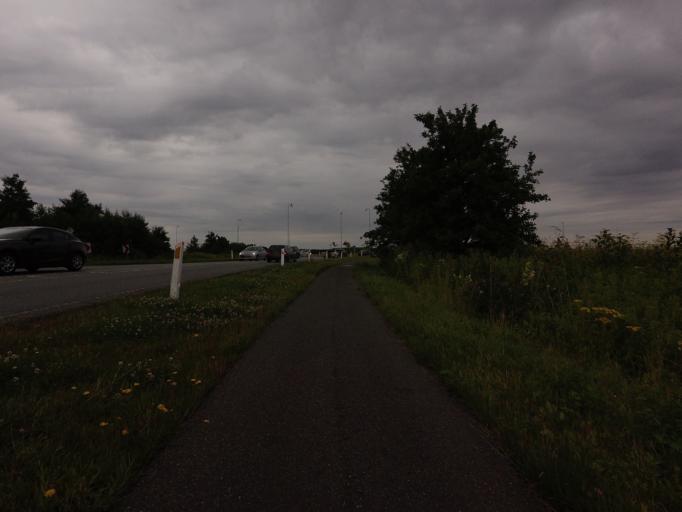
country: DK
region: North Denmark
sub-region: Alborg Kommune
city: Vadum
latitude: 57.1012
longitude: 9.8851
